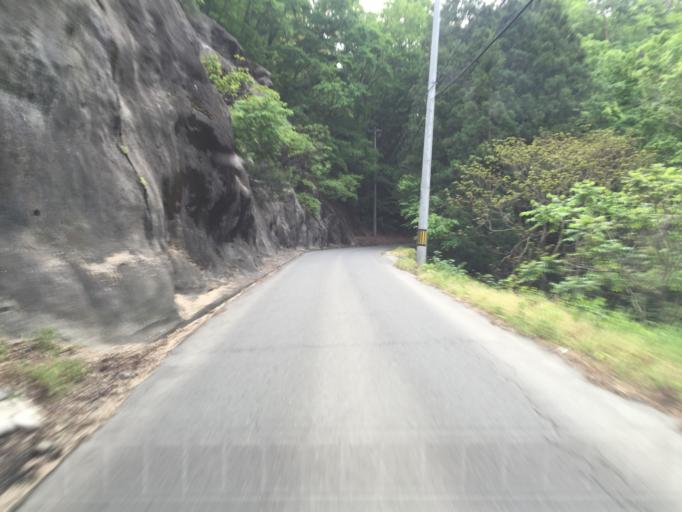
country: JP
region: Fukushima
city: Yanagawamachi-saiwaicho
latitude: 37.8979
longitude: 140.6652
